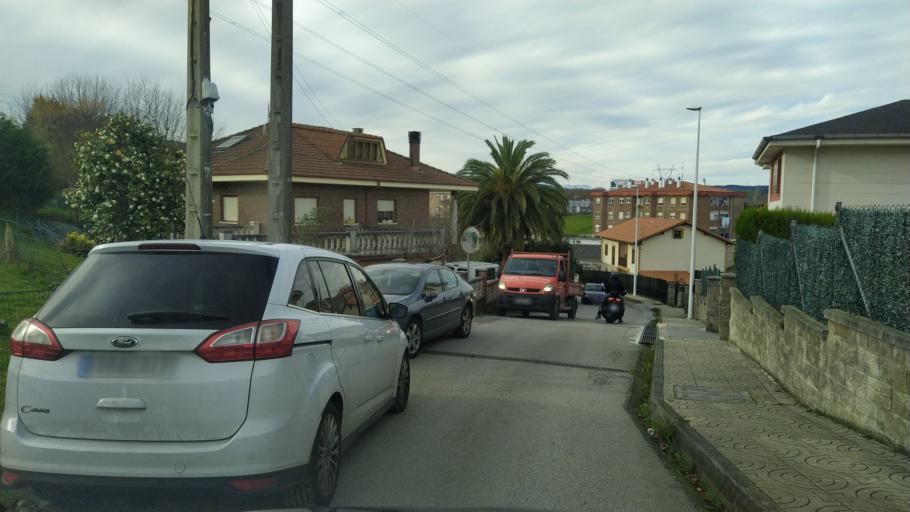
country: ES
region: Cantabria
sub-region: Provincia de Cantabria
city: Reocin
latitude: 43.3553
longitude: -4.0870
